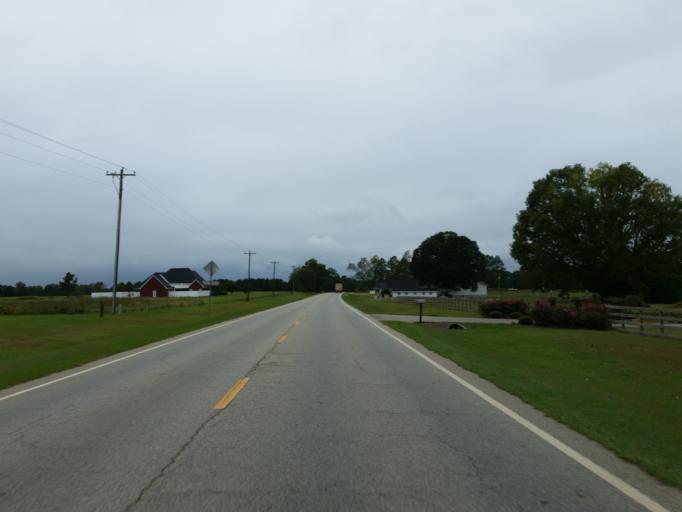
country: US
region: Georgia
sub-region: Cook County
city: Adel
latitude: 31.1311
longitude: -83.3572
